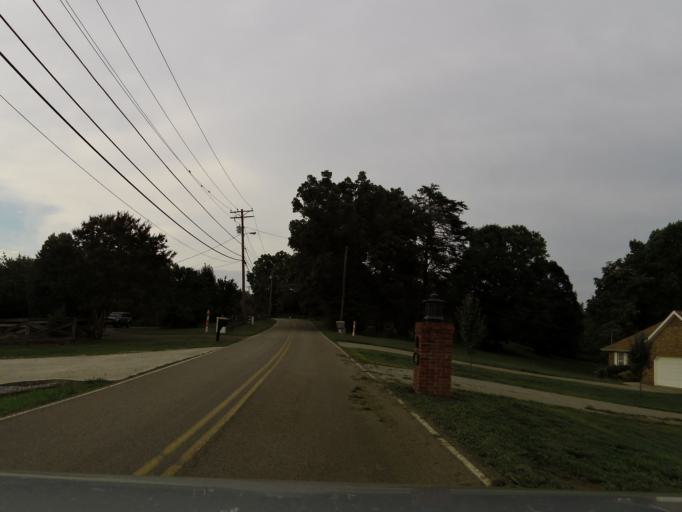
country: US
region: Tennessee
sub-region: Knox County
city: Knoxville
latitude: 35.8822
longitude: -83.9444
